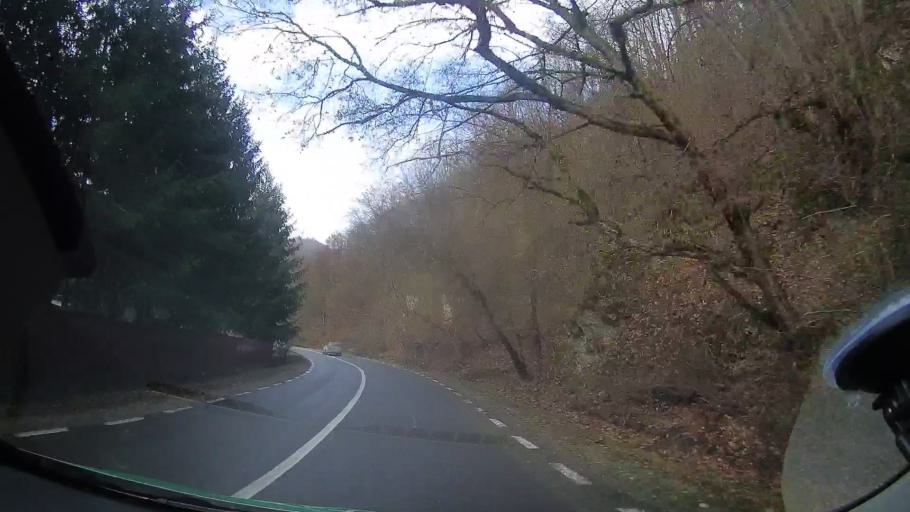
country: RO
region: Cluj
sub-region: Comuna Valea Ierii
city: Valea Ierii
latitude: 46.6141
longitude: 23.4048
